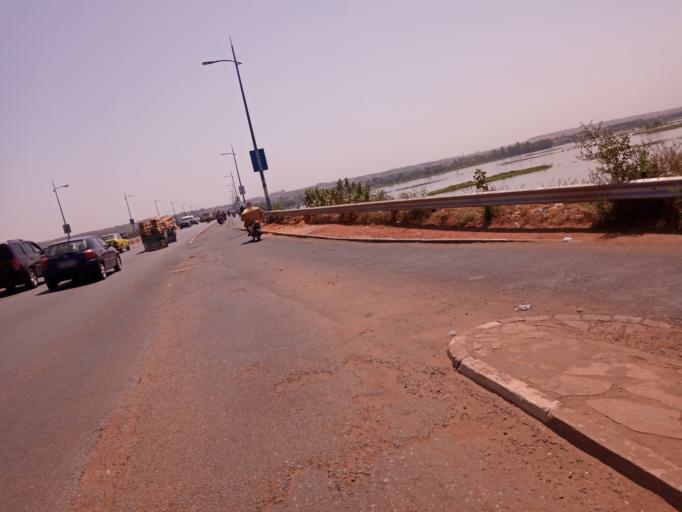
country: ML
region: Bamako
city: Bamako
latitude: 12.6269
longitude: -8.0074
